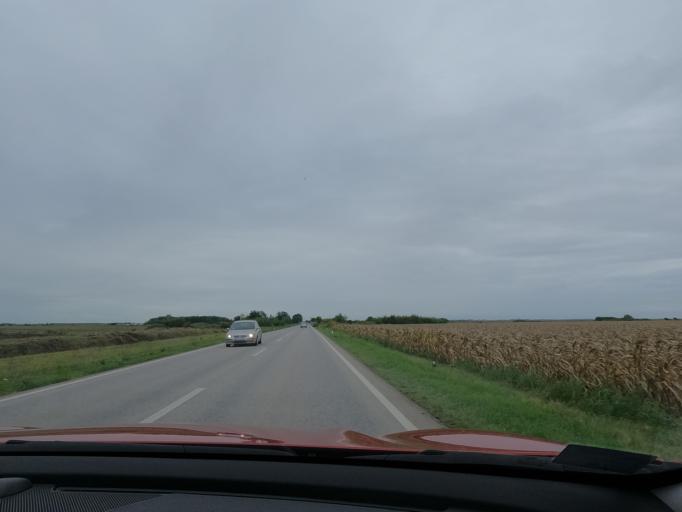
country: RS
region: Autonomna Pokrajina Vojvodina
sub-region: Severnobanatski Okrug
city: Kikinda
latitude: 45.7618
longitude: 20.4228
